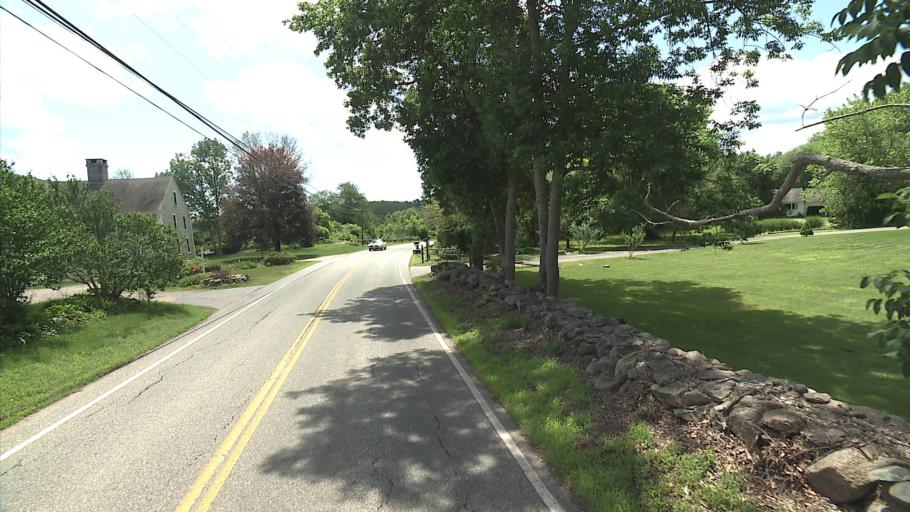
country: US
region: Connecticut
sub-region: New London County
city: Old Mystic
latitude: 41.4417
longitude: -71.9094
